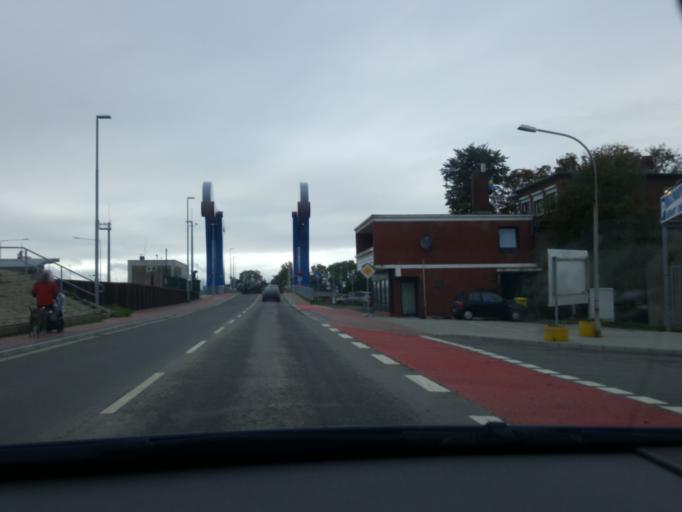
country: DE
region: Lower Saxony
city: Emden
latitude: 53.3445
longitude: 7.1910
